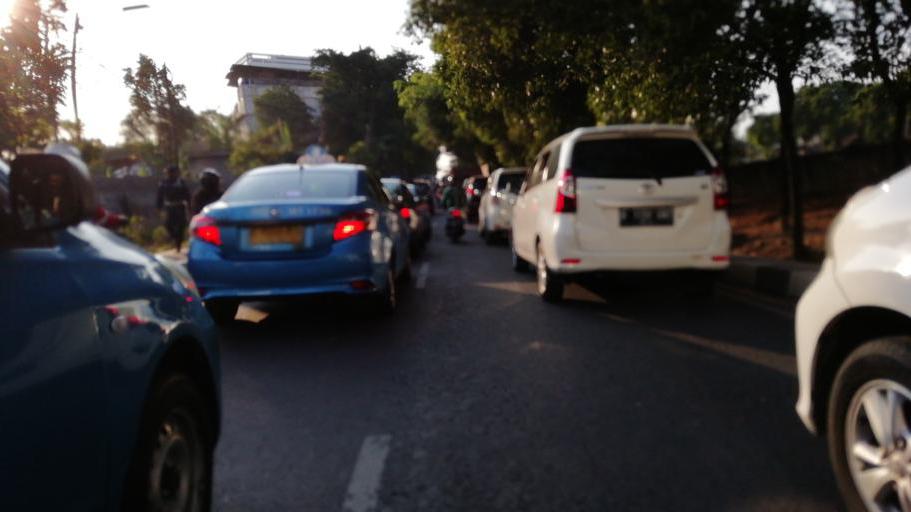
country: ID
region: Jakarta Raya
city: Jakarta
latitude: -6.2973
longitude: 106.8291
